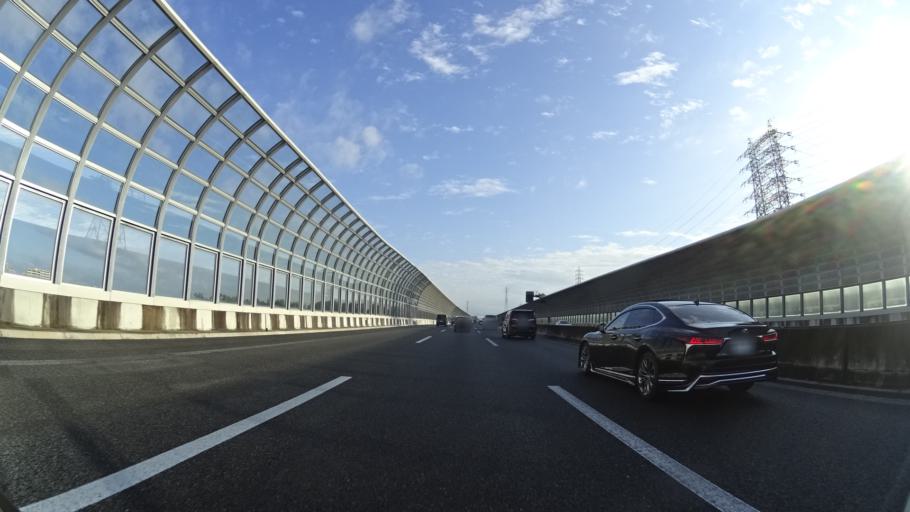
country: JP
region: Osaka
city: Neyagawa
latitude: 34.7658
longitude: 135.6533
